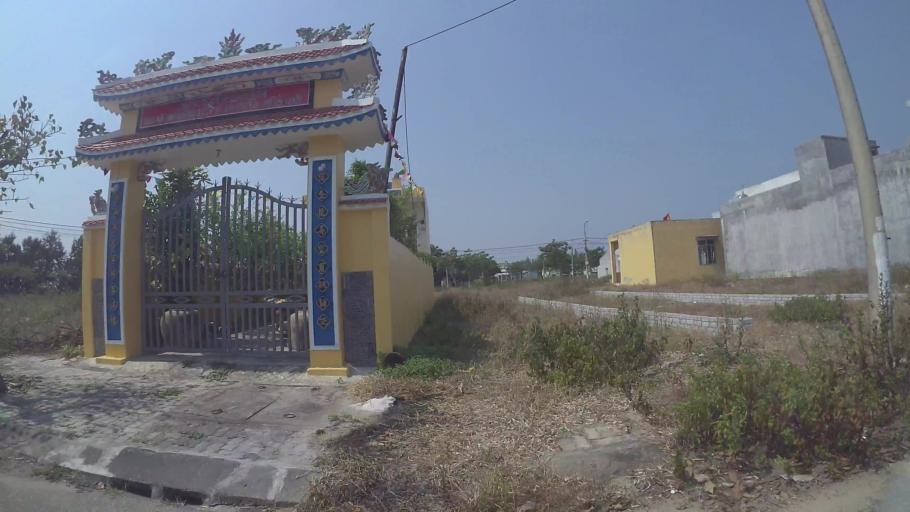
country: VN
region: Da Nang
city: Ngu Hanh Son
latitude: 15.9790
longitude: 108.2698
